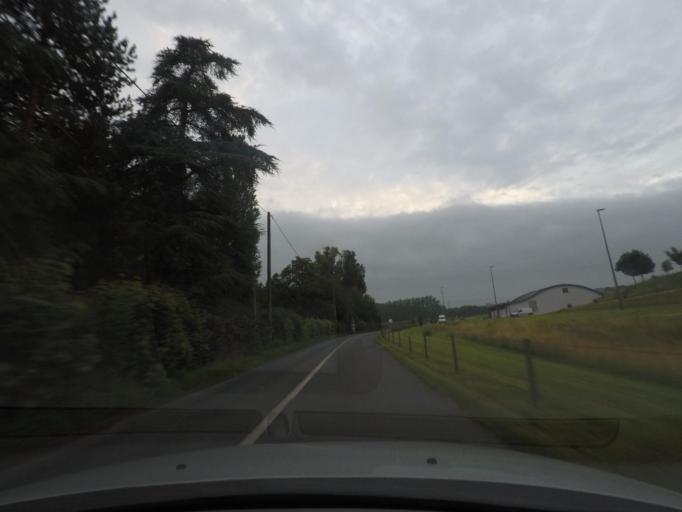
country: FR
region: Haute-Normandie
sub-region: Departement de la Seine-Maritime
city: Fontaine-le-Bourg
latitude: 49.5603
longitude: 1.1504
